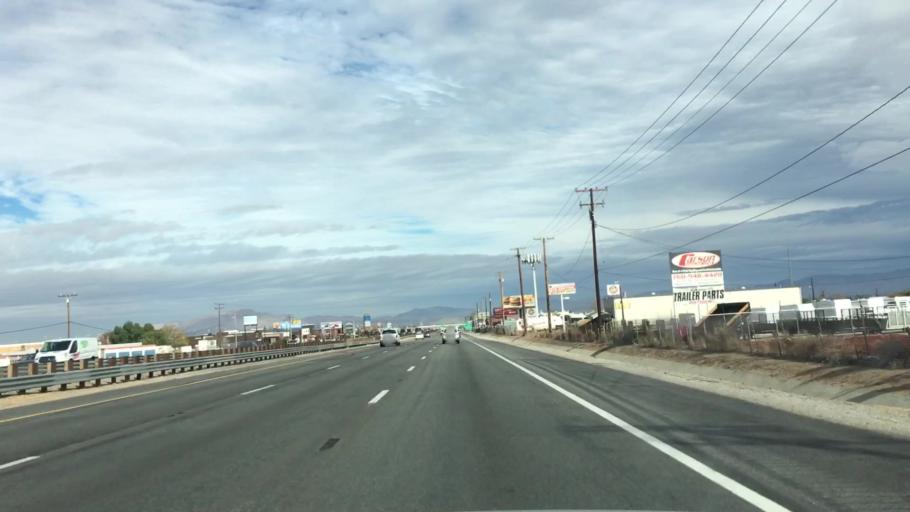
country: US
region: California
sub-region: San Bernardino County
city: Mountain View Acres
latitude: 34.4587
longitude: -117.3552
